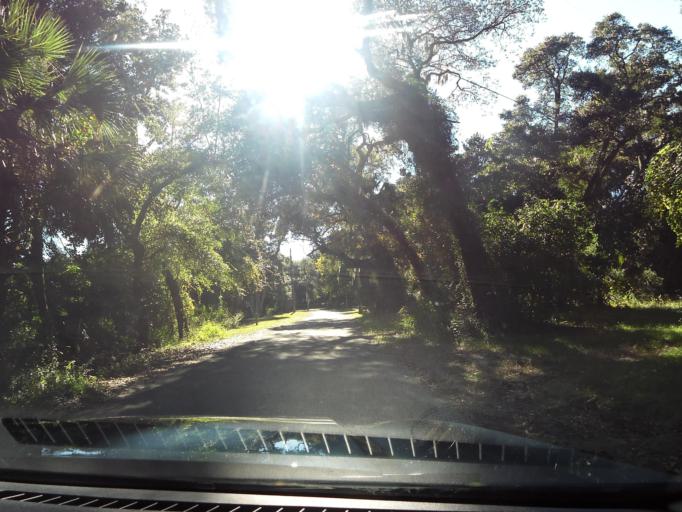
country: US
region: Florida
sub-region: Duval County
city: Atlantic Beach
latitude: 30.4253
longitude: -81.4270
